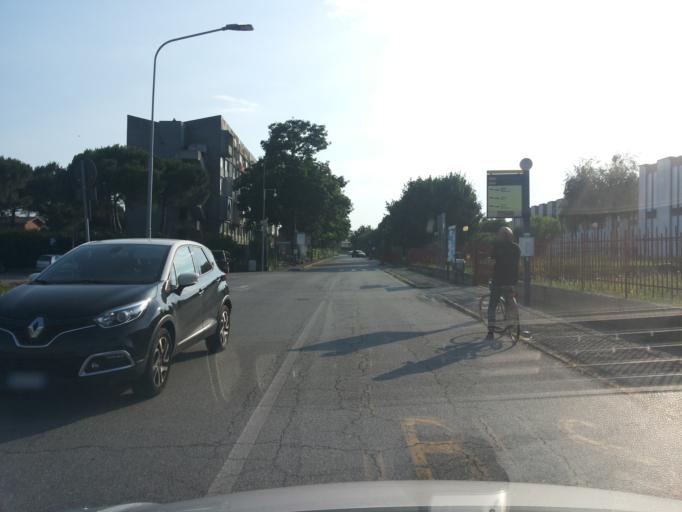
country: IT
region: Piedmont
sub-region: Provincia di Vercelli
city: Santhia
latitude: 45.3721
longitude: 8.1650
